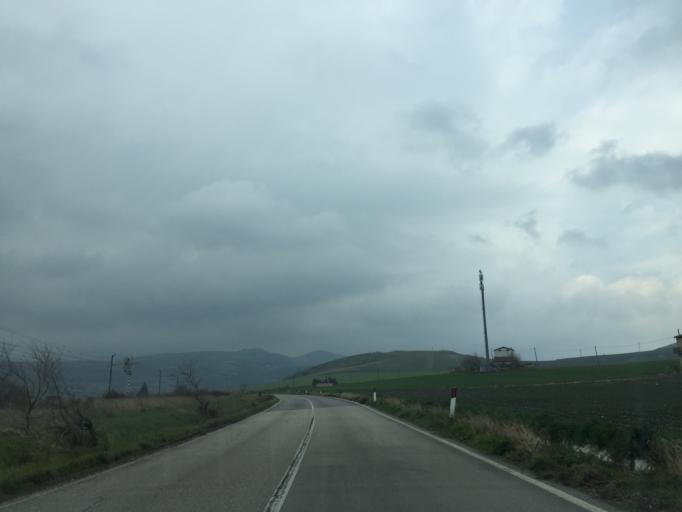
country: IT
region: Apulia
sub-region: Provincia di Foggia
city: Bovino
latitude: 41.2900
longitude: 15.3810
